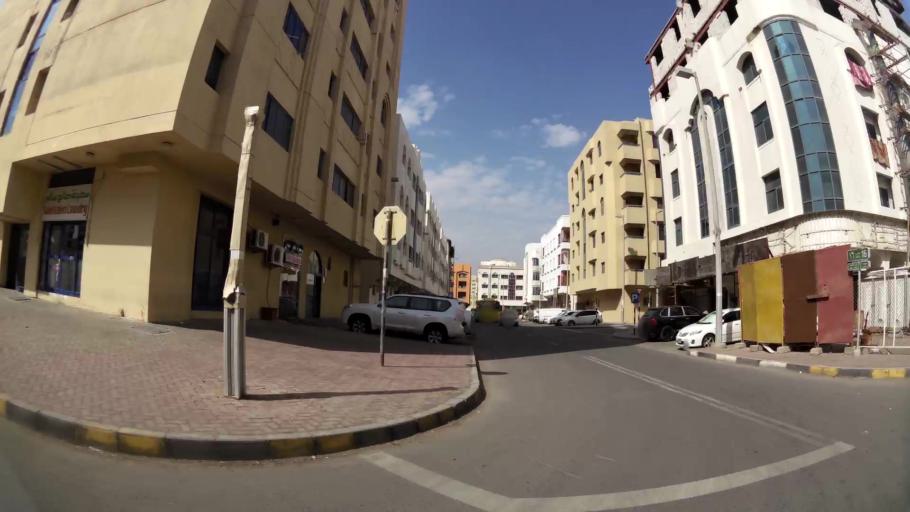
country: AE
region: Abu Dhabi
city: Abu Dhabi
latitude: 24.3363
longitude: 54.5369
